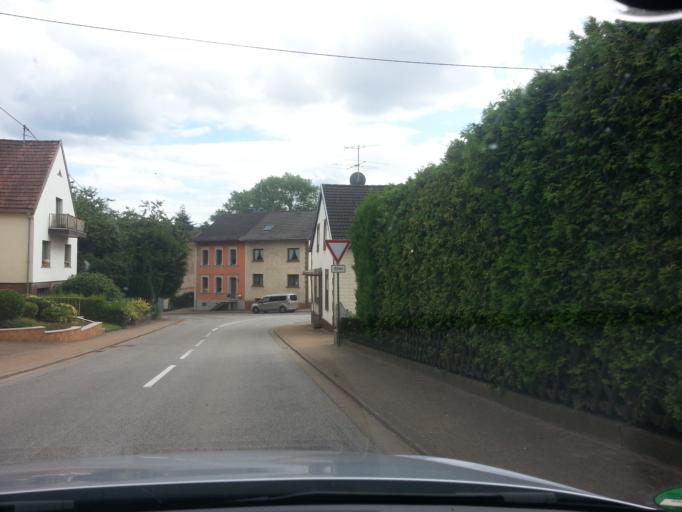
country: DE
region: Saarland
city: Nalbach
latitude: 49.4172
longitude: 6.7638
